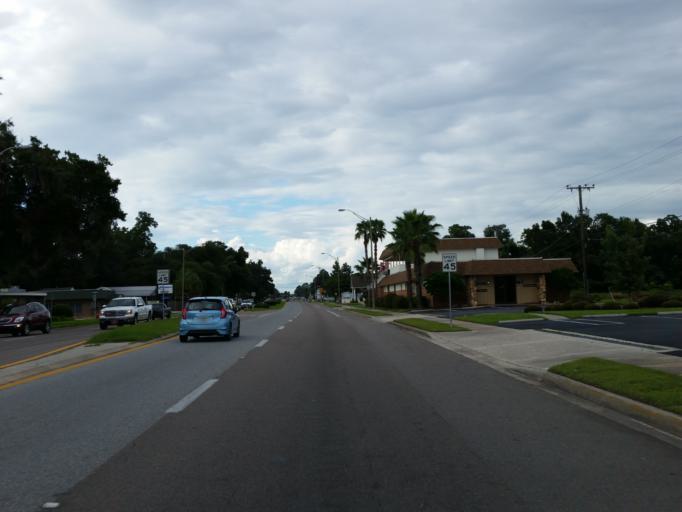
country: US
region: Florida
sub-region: Columbia County
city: Lake City
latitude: 30.1790
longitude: -82.6392
